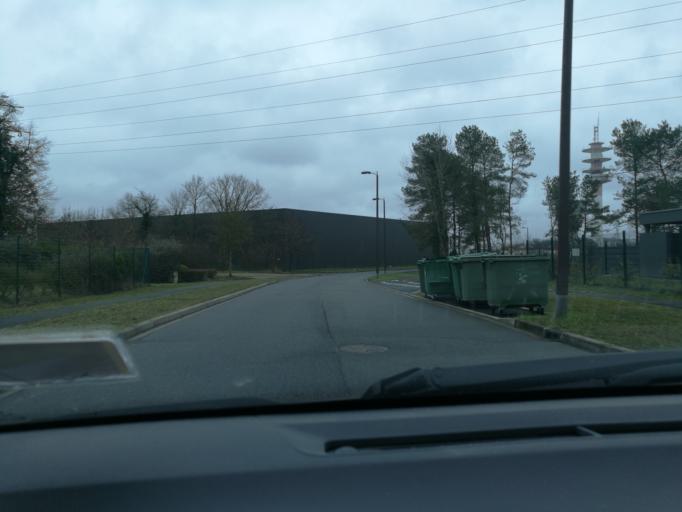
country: FR
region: Centre
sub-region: Departement du Loiret
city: Fleury-les-Aubrais
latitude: 47.9469
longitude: 1.9281
